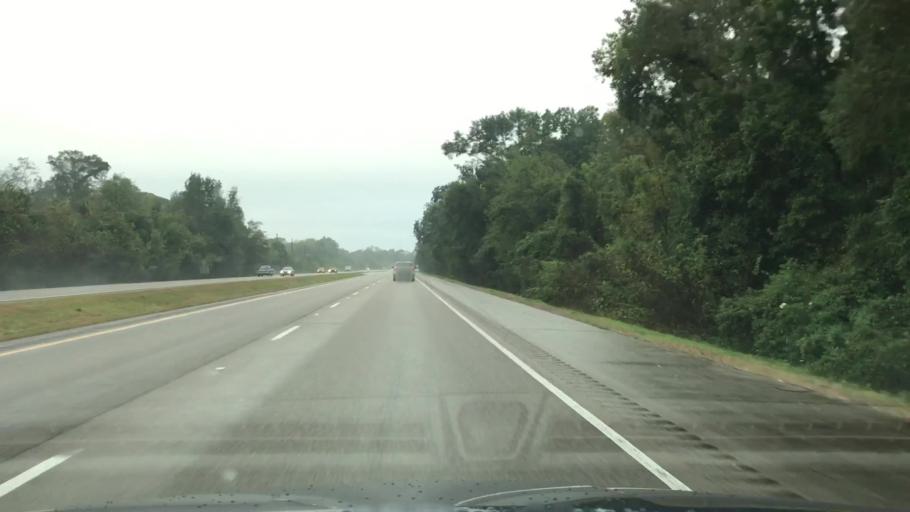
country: US
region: Louisiana
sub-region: Saint Charles Parish
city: Paradis
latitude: 29.8500
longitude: -90.4479
